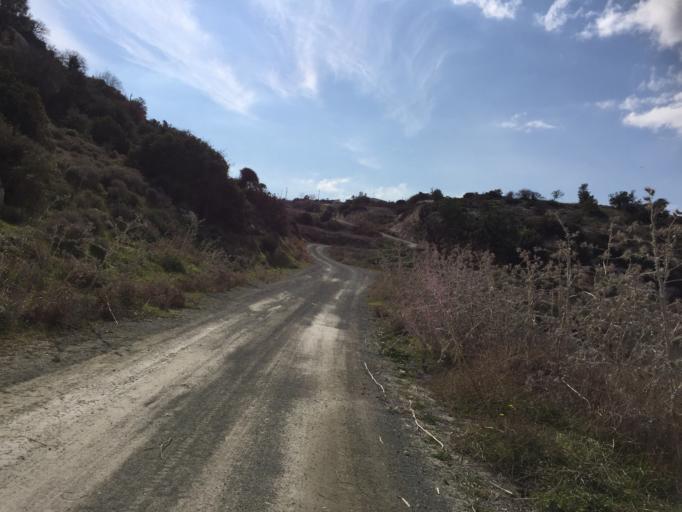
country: CY
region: Larnaka
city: Agios Tychon
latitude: 34.7474
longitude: 33.1331
